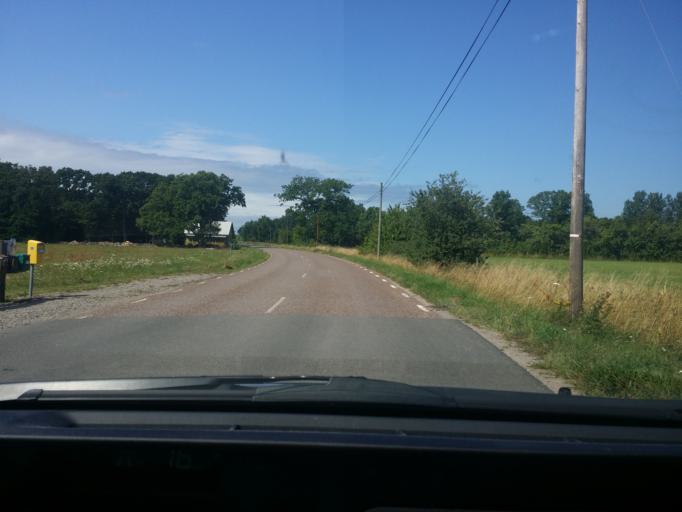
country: SE
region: Kalmar
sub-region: Borgholms Kommun
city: Borgholm
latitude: 57.2097
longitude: 16.9739
